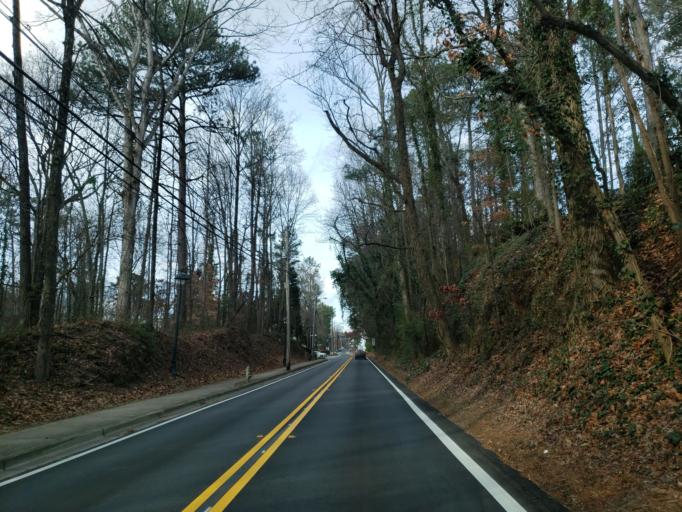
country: US
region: Georgia
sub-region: Fulton County
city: Sandy Springs
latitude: 33.9171
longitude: -84.3871
